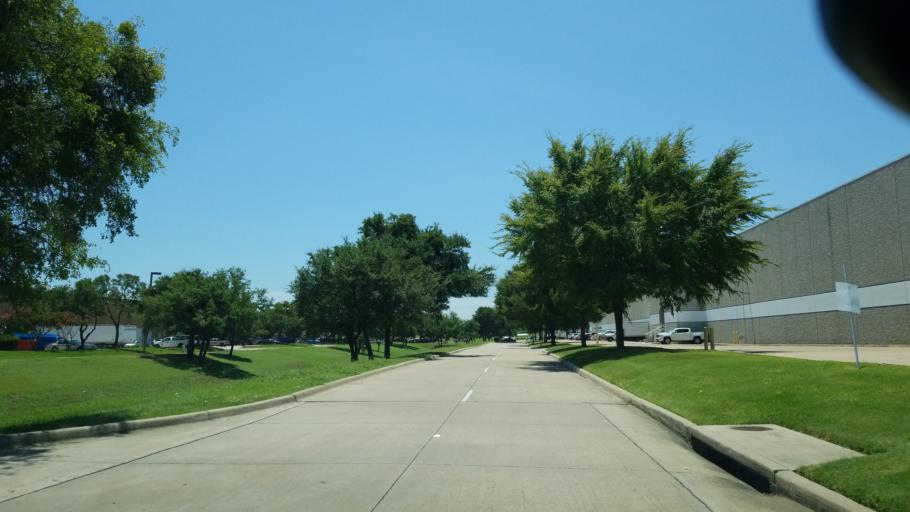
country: US
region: Texas
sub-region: Dallas County
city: Farmers Branch
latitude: 32.9286
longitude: -96.9223
